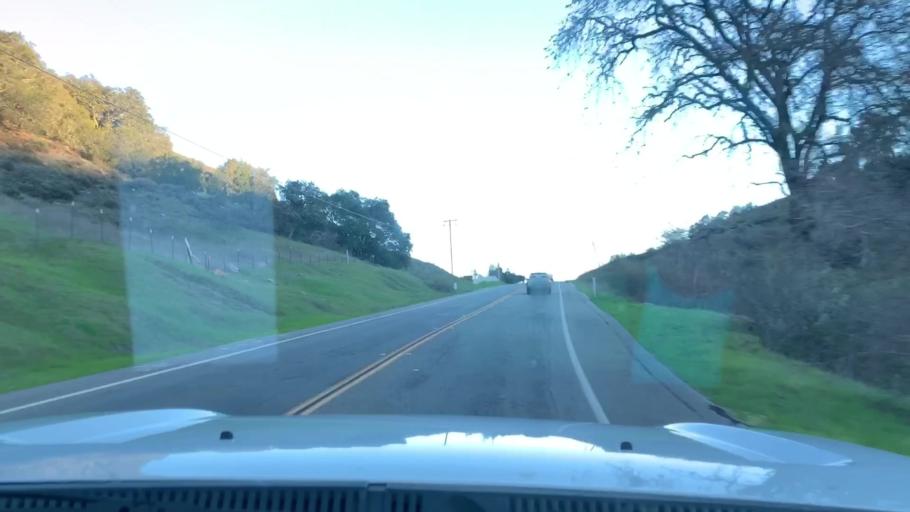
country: US
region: California
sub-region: San Luis Obispo County
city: Atascadero
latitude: 35.4590
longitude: -120.7195
